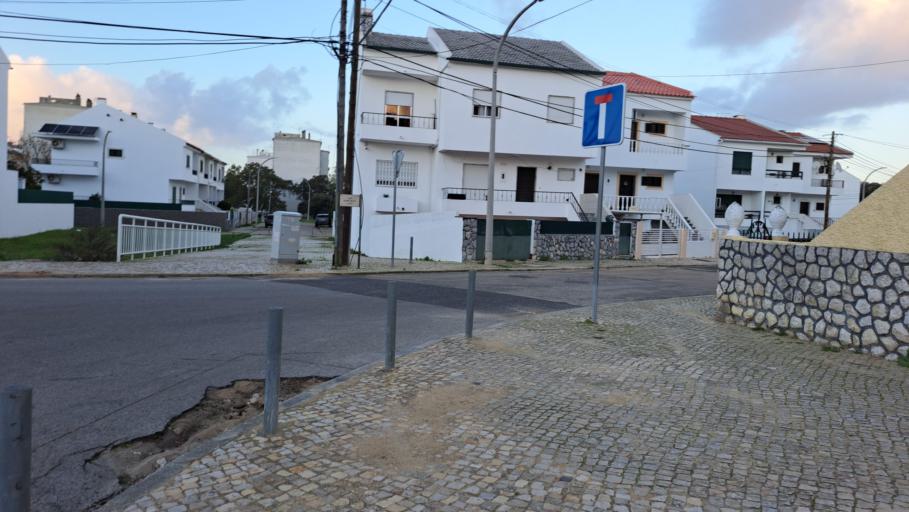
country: PT
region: Setubal
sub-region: Moita
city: Alhos Vedros
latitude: 38.6465
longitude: -9.0361
